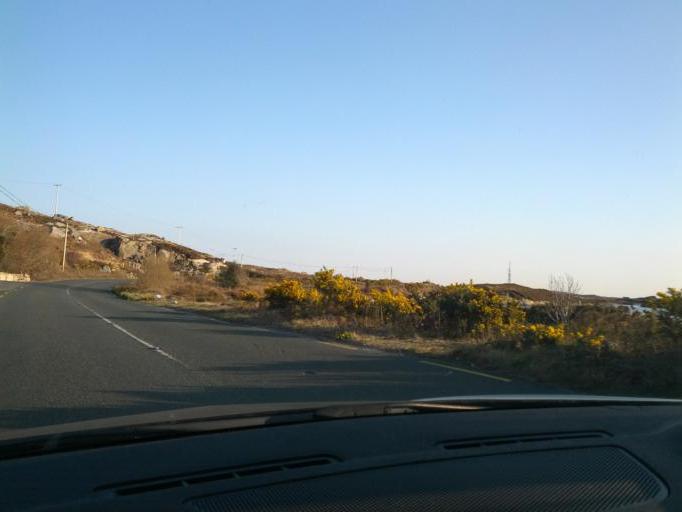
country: IE
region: Connaught
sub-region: County Galway
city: Oughterard
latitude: 53.3040
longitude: -9.5558
